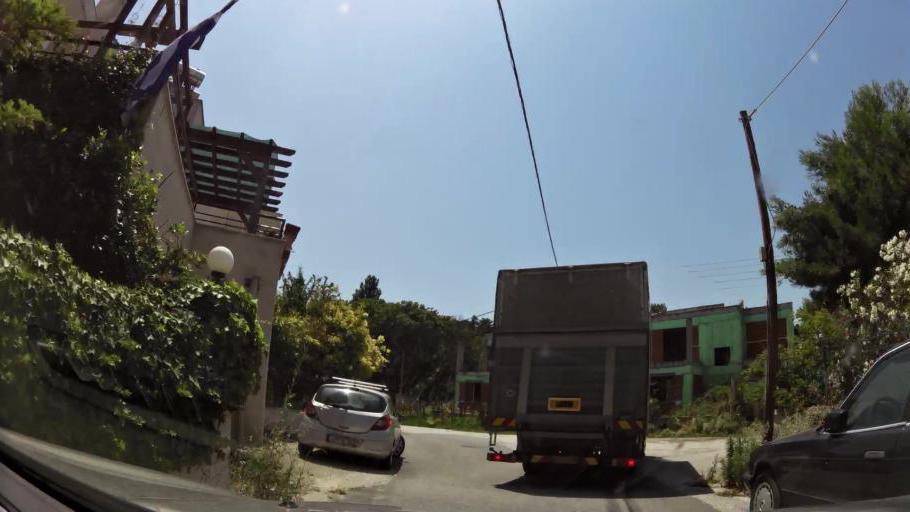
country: GR
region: Central Macedonia
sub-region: Nomos Thessalonikis
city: Trilofos
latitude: 40.4636
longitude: 22.9706
